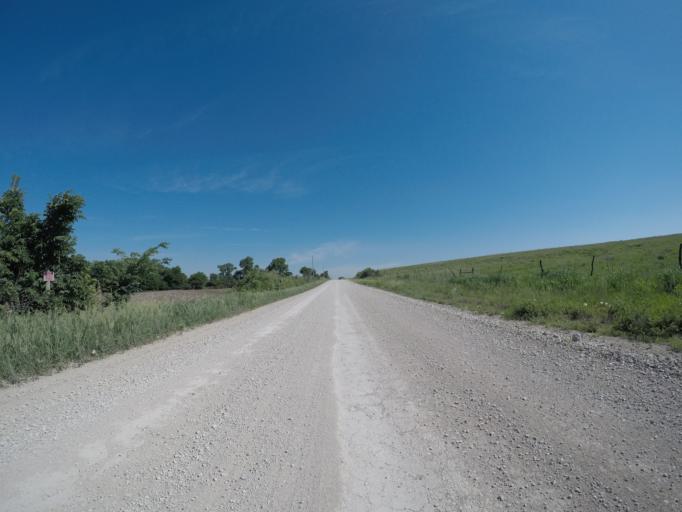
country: US
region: Kansas
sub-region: Wabaunsee County
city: Alma
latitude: 38.9966
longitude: -96.1137
